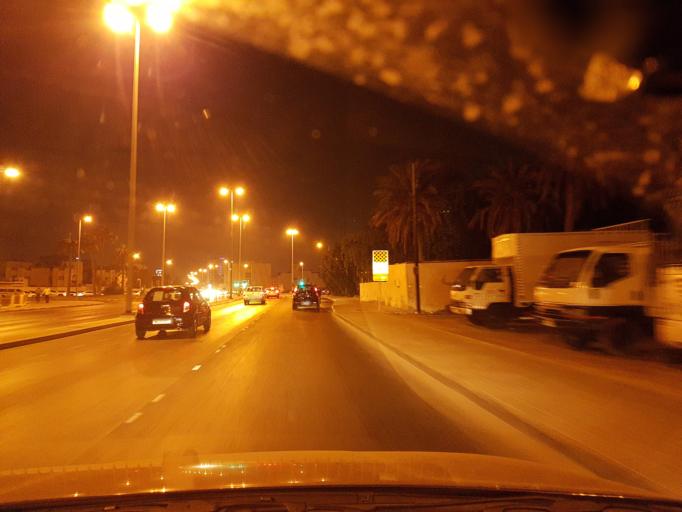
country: BH
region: Manama
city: Manama
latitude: 26.2191
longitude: 50.5774
